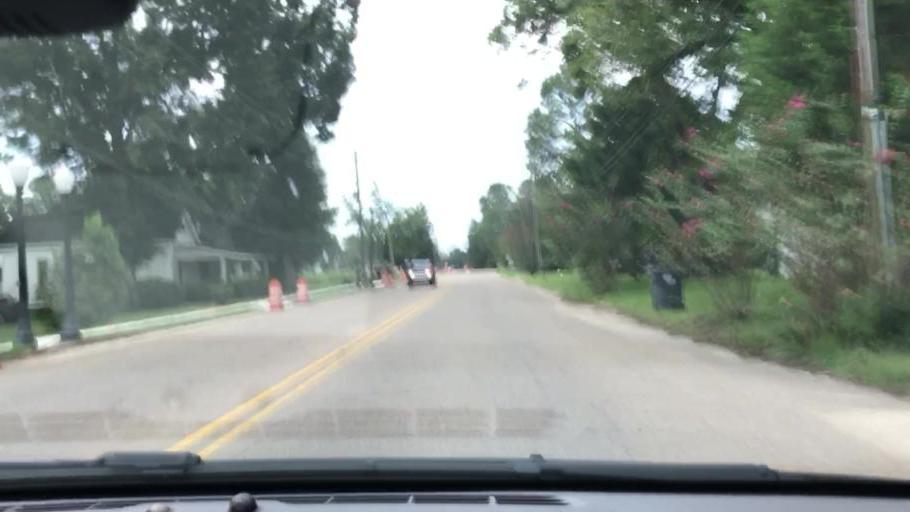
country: US
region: Alabama
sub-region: Houston County
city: Ashford
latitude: 31.1811
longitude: -85.2372
